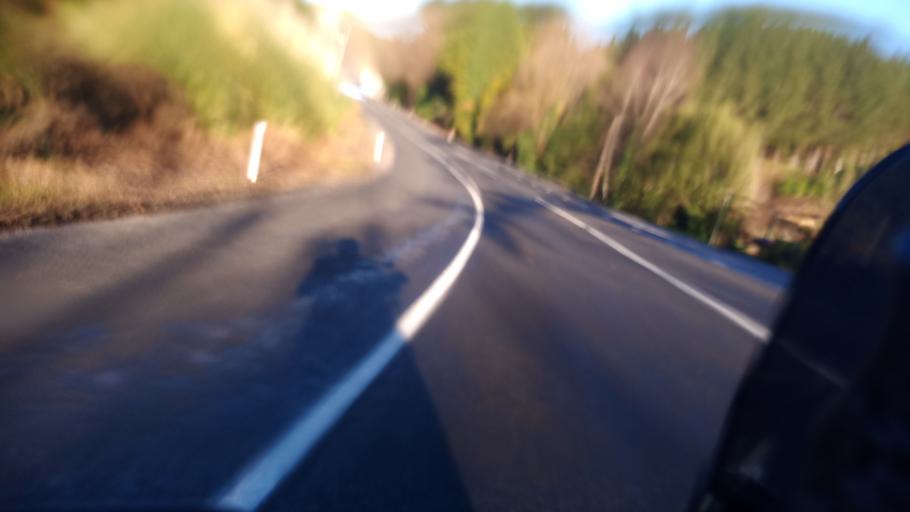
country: NZ
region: Hawke's Bay
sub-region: Wairoa District
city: Wairoa
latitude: -39.0147
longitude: 177.3346
